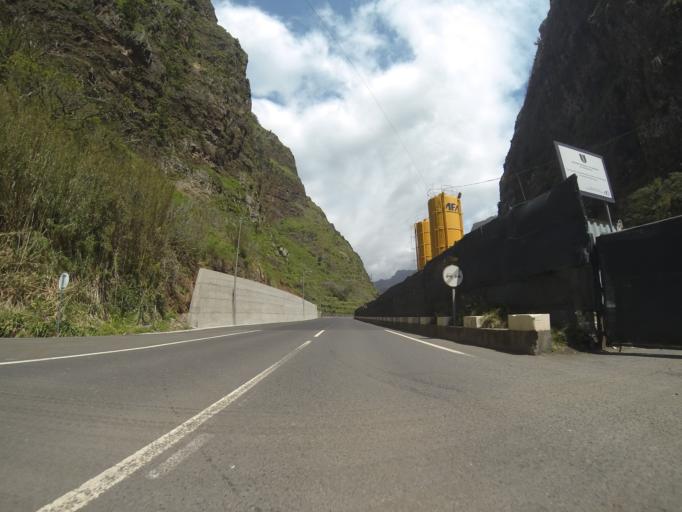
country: PT
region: Madeira
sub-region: Ribeira Brava
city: Campanario
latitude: 32.7044
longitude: -17.0391
